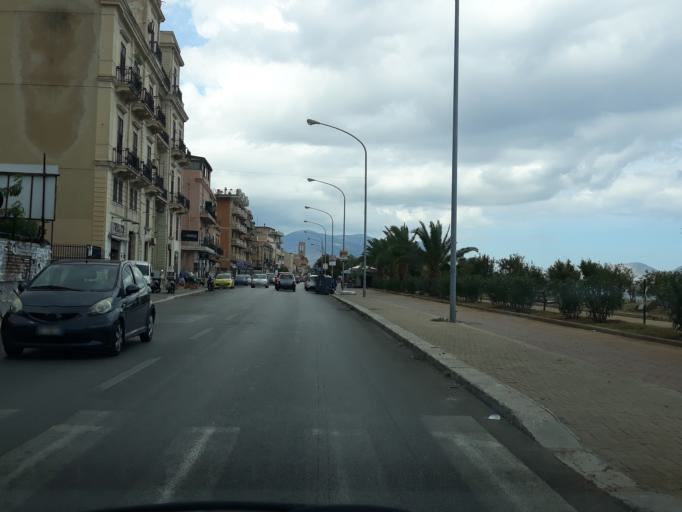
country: IT
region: Sicily
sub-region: Palermo
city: Ciaculli
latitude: 38.1036
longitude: 13.3928
